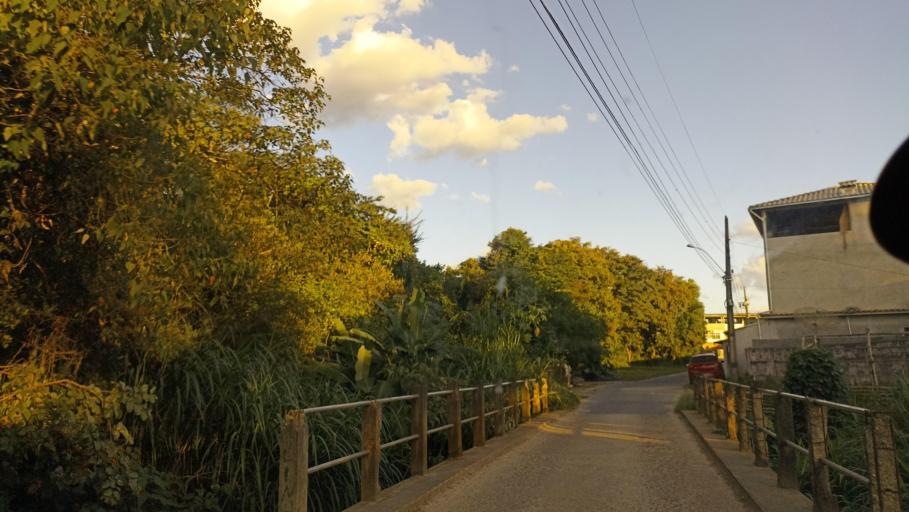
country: BR
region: Minas Gerais
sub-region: Sao Joao Del Rei
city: Sao Joao del Rei
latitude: -21.1845
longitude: -44.3321
